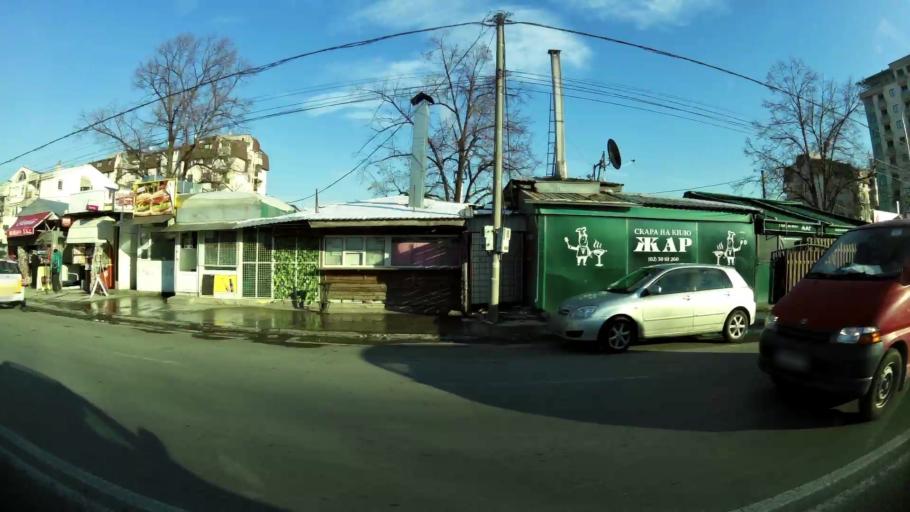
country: MK
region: Karpos
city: Skopje
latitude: 42.0013
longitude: 21.3897
